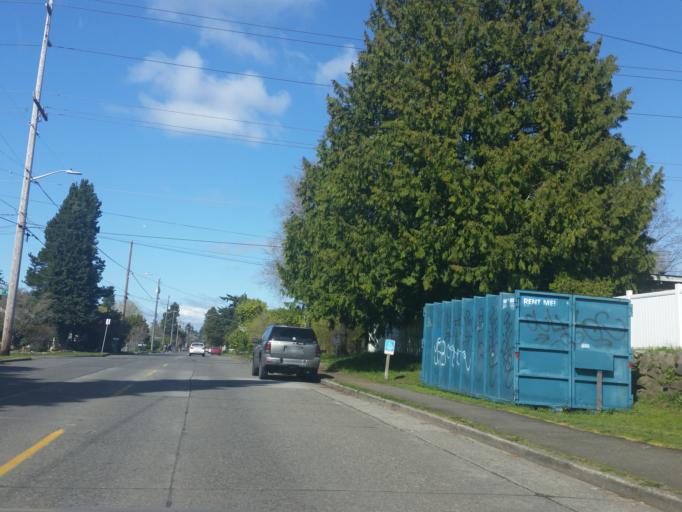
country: US
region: Washington
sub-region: King County
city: Shoreline
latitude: 47.6974
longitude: -122.3607
